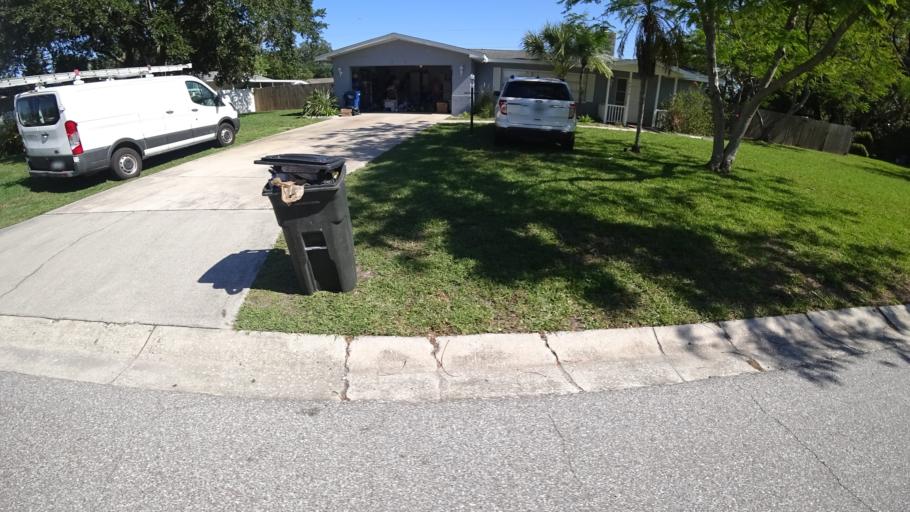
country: US
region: Florida
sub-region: Manatee County
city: West Bradenton
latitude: 27.4804
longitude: -82.6108
